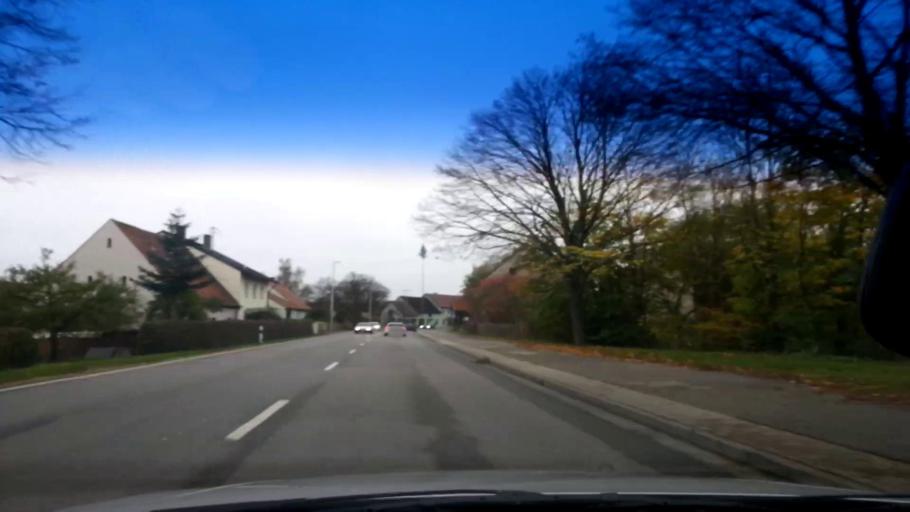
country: DE
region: Bavaria
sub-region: Upper Franconia
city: Walsdorf
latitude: 49.8296
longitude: 10.7918
